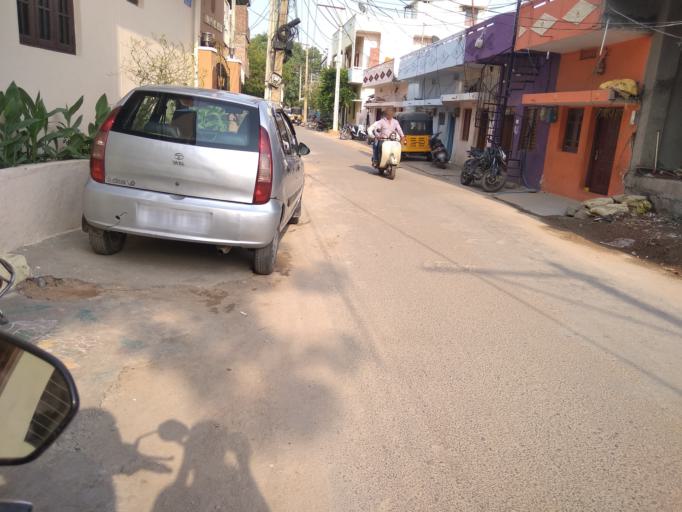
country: IN
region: Telangana
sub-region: Hyderabad
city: Malkajgiri
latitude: 17.4611
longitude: 78.5536
